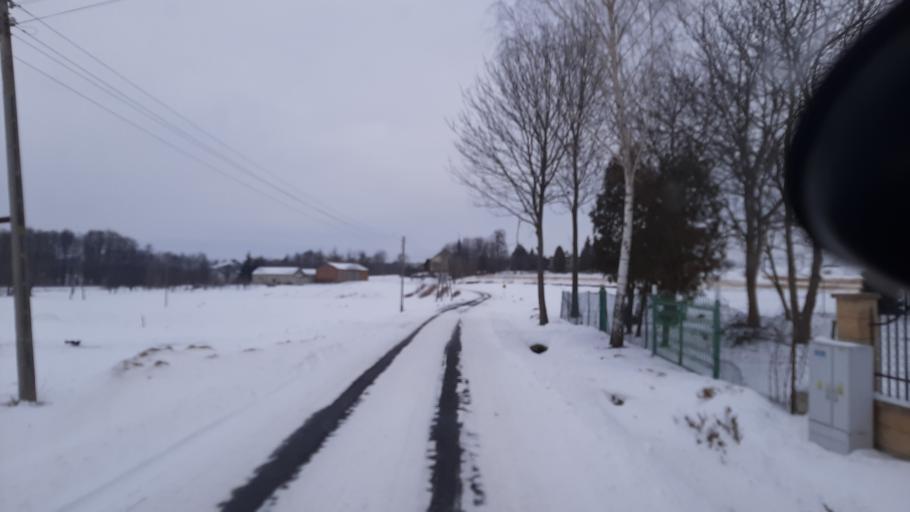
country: PL
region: Lublin Voivodeship
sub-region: Powiat lubelski
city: Garbow
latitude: 51.3402
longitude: 22.2938
